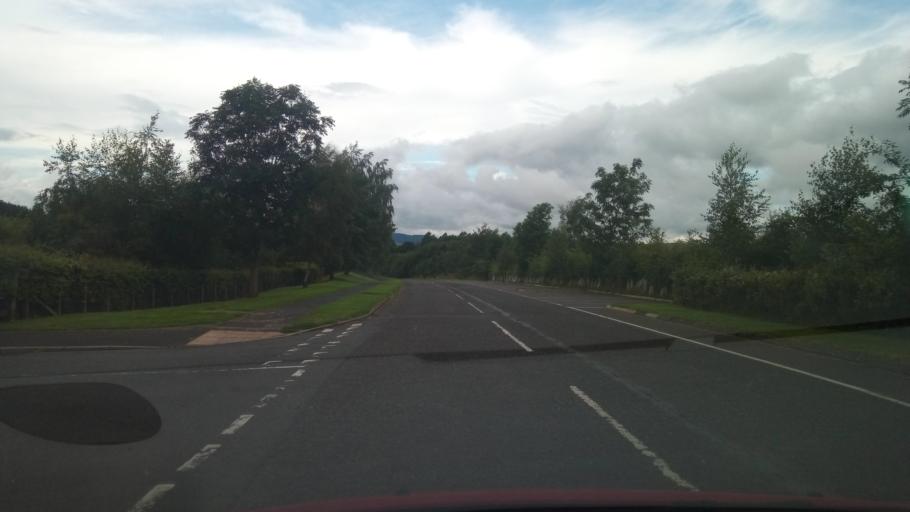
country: GB
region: Scotland
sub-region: The Scottish Borders
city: Melrose
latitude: 55.5969
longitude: -2.7048
